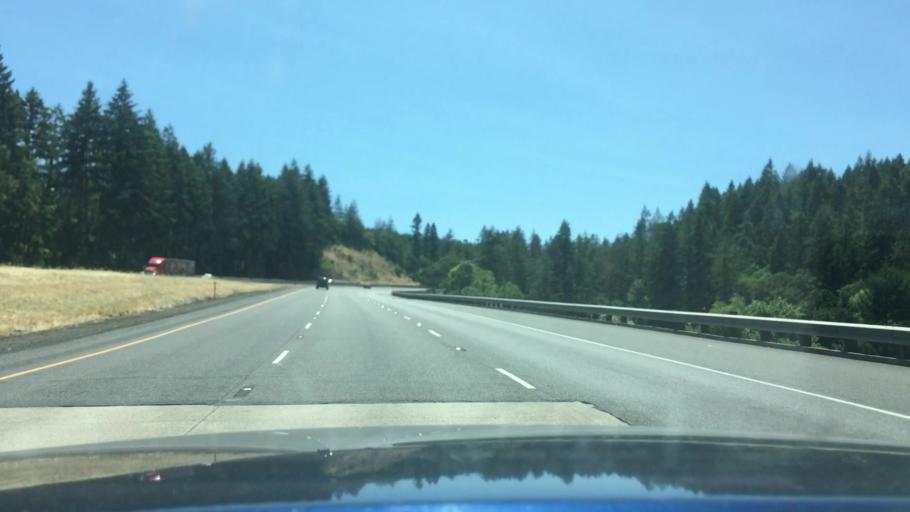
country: US
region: Oregon
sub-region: Douglas County
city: Yoncalla
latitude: 43.5306
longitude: -123.3006
